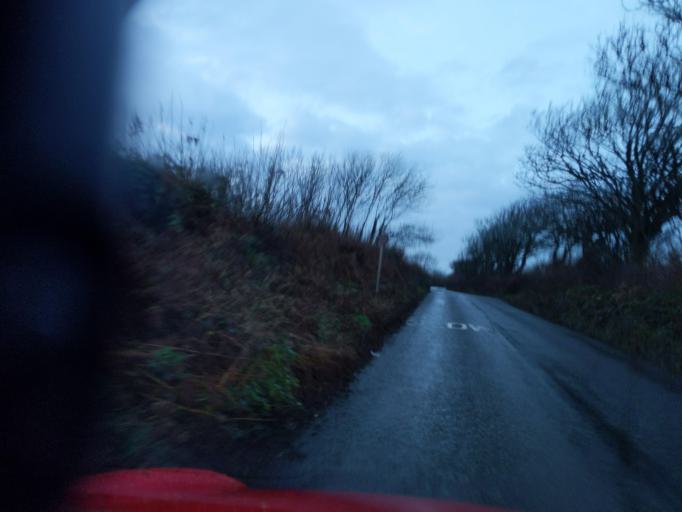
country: GB
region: England
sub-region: Devon
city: Wembury
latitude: 50.3327
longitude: -4.0654
